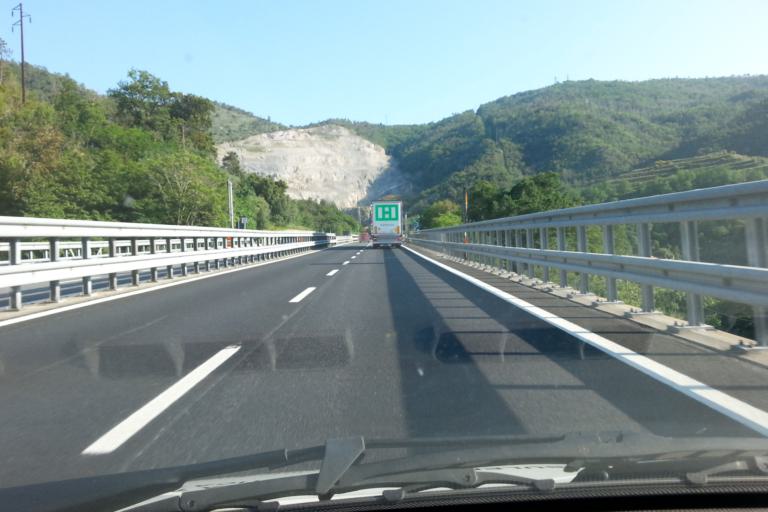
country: IT
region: Liguria
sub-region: Provincia di Savona
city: Valle di Vado
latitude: 44.2557
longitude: 8.4068
